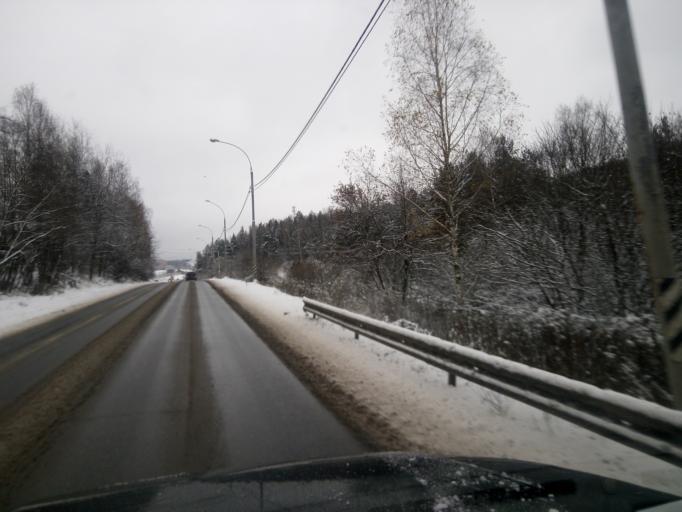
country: RU
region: Moskovskaya
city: Skhodnya
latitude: 55.9653
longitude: 37.3097
